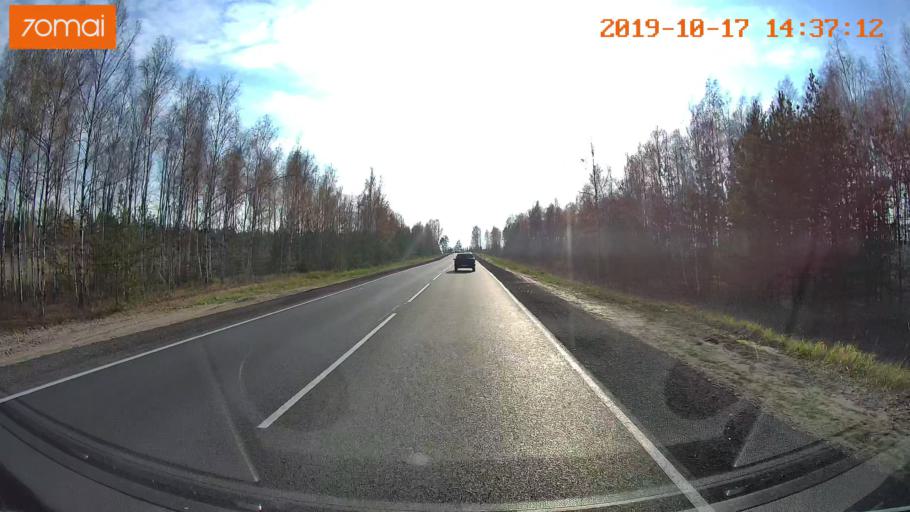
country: RU
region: Rjazan
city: Solotcha
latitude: 54.8820
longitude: 39.9979
